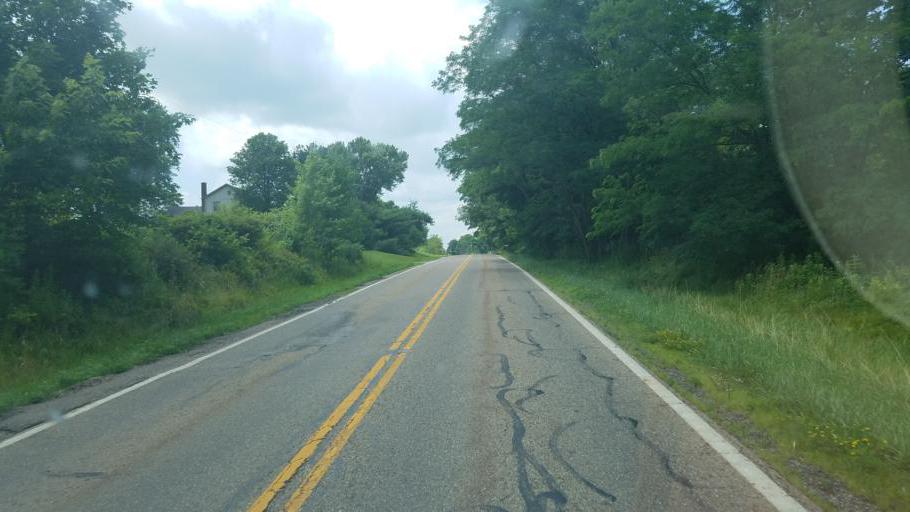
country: US
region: Ohio
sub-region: Stark County
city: Minerva
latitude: 40.7885
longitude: -80.9883
